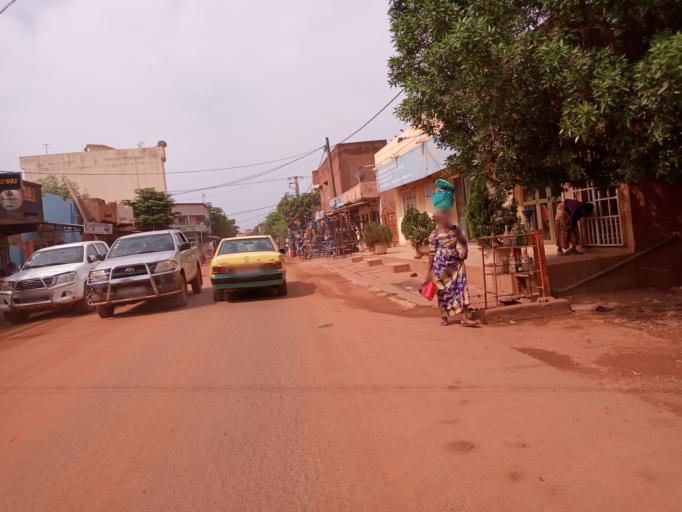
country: ML
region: Bamako
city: Bamako
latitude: 12.5644
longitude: -7.9900
